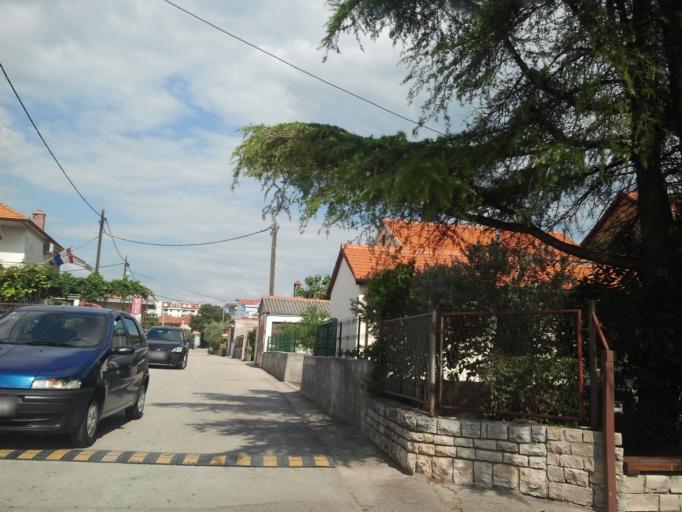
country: HR
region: Zadarska
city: Zadar
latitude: 44.1192
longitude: 15.2504
